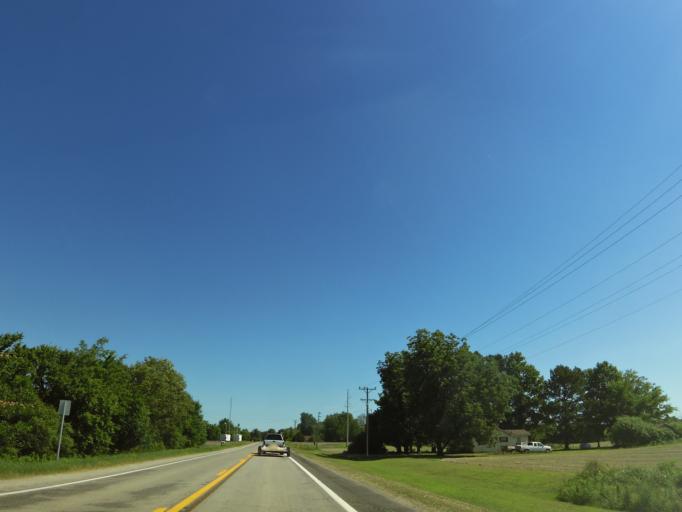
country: US
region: Arkansas
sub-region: Clay County
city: Piggott
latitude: 36.4446
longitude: -90.1472
